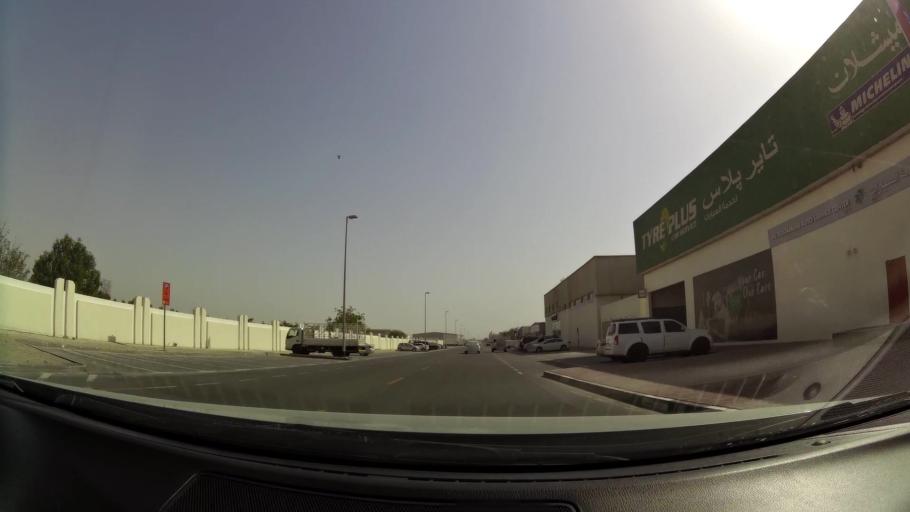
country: AE
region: Dubai
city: Dubai
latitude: 25.1670
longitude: 55.2402
